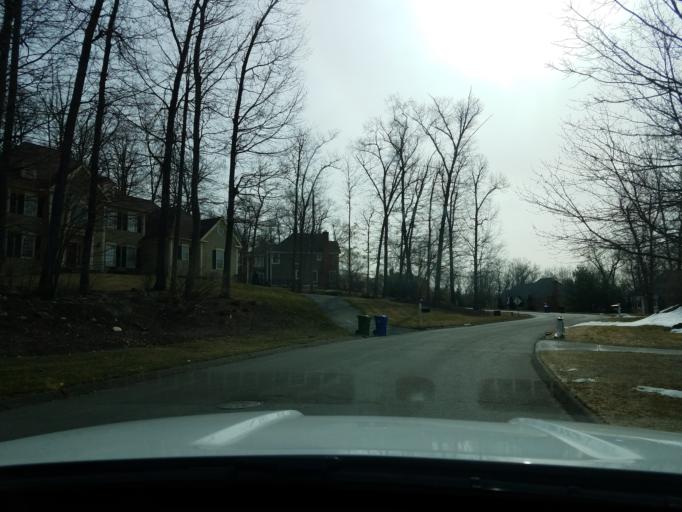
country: US
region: Connecticut
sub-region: Hartford County
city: Collinsville
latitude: 41.7852
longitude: -72.9025
